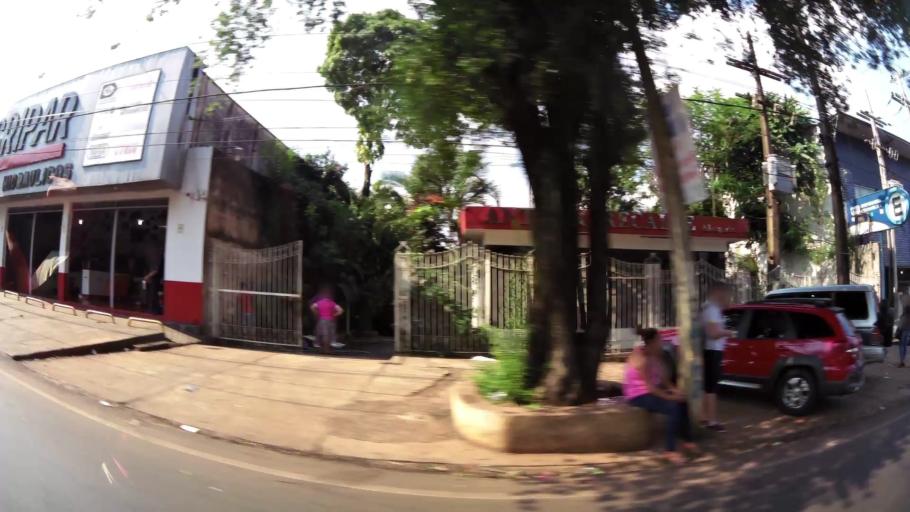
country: PY
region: Alto Parana
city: Ciudad del Este
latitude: -25.5084
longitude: -54.6330
